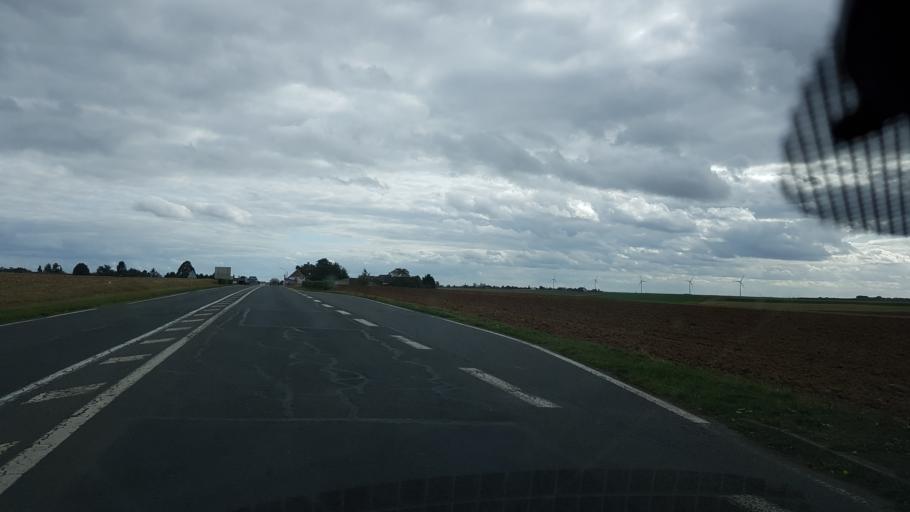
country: FR
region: Centre
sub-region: Departement du Loiret
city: Pithiviers
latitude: 48.2294
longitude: 2.2275
